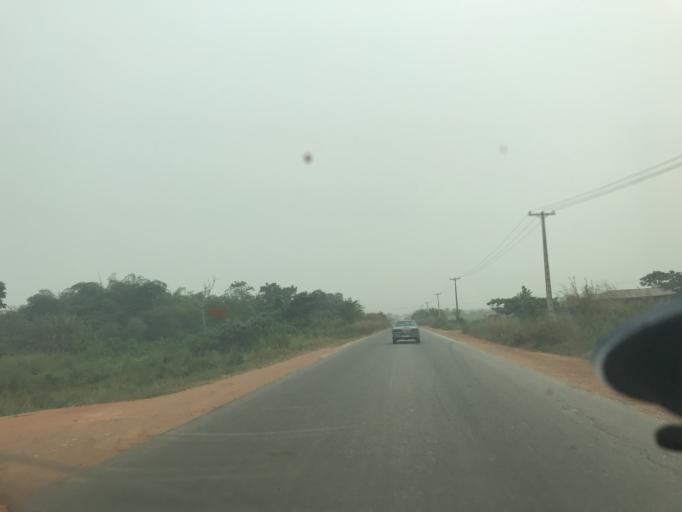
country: NG
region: Ogun
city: Itori
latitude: 6.8900
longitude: 3.1605
